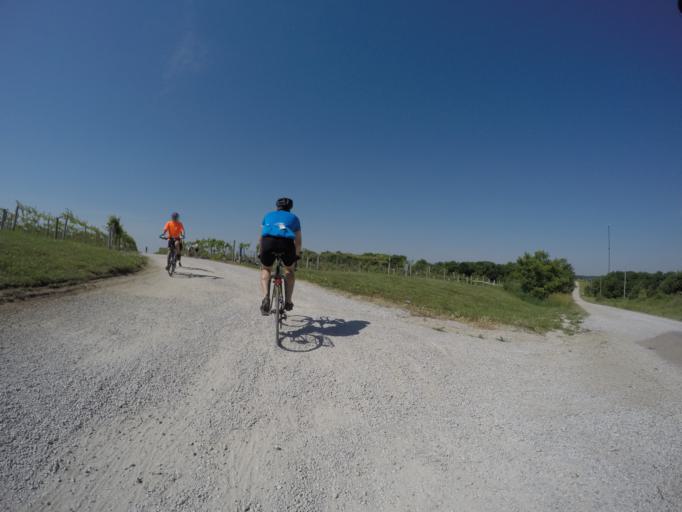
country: US
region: Nebraska
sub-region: Pawnee County
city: Pawnee City
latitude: 40.1167
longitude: -96.1627
